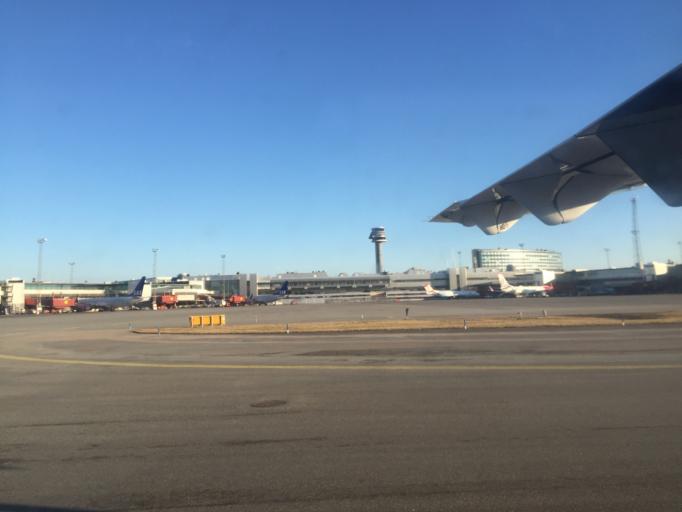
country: SE
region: Stockholm
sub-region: Sigtuna Kommun
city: Marsta
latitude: 59.6538
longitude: 17.9258
